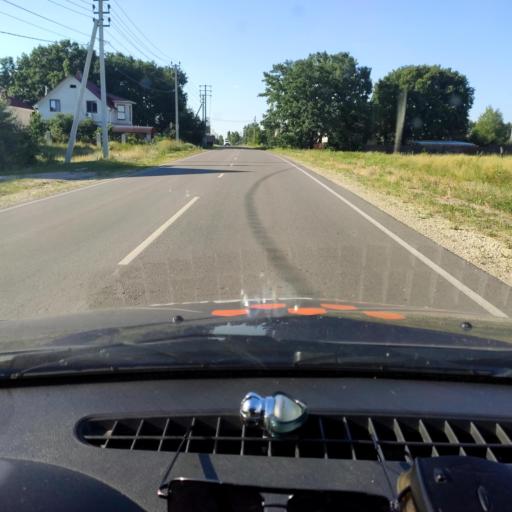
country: RU
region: Voronezj
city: Podgornoye
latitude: 51.8723
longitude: 39.1731
